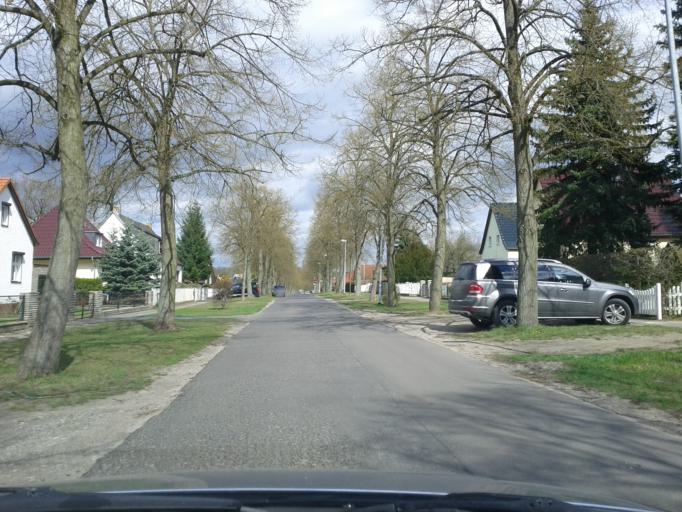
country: DE
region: Brandenburg
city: Schoneiche
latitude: 52.4723
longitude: 13.7013
